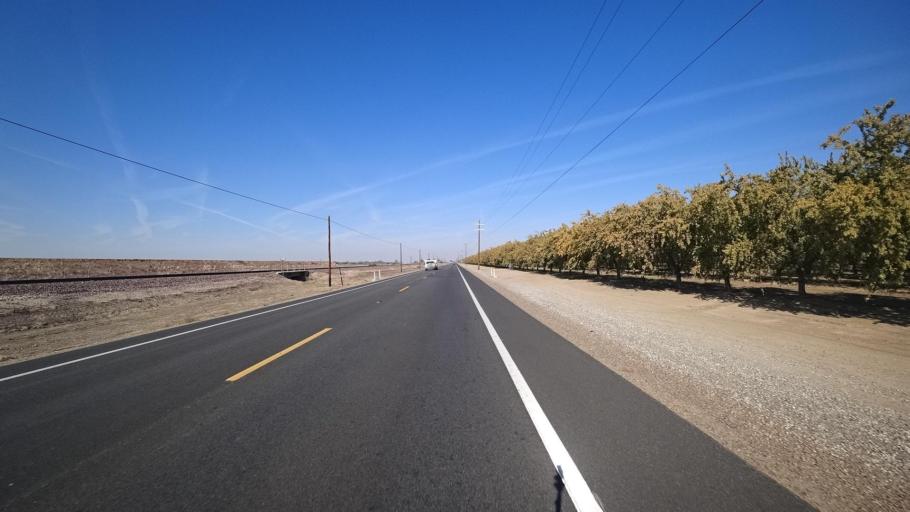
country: US
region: California
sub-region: Kern County
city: Wasco
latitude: 35.6477
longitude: -119.3310
